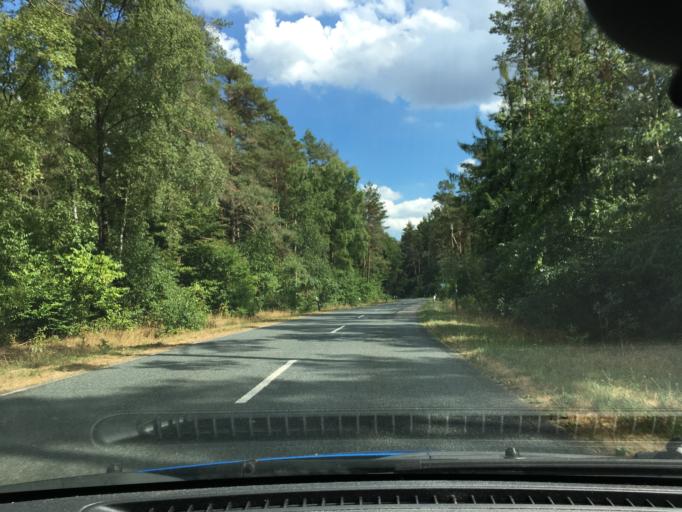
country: DE
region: Lower Saxony
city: Rehlingen
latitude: 53.0820
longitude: 10.2199
